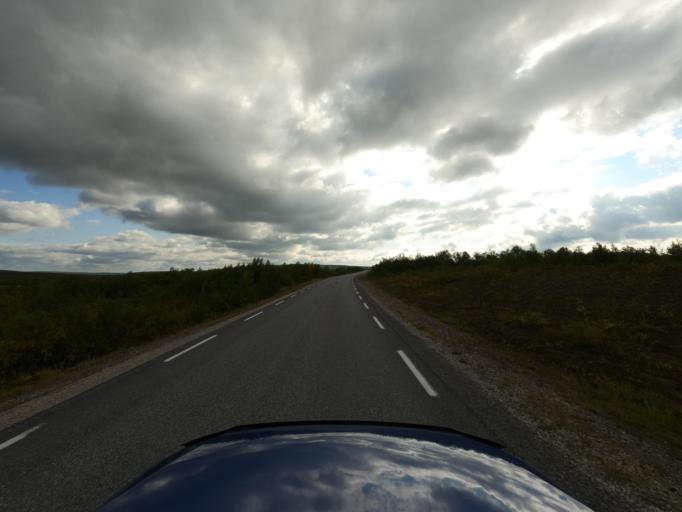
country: NO
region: Finnmark Fylke
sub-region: Porsanger
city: Lakselv
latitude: 69.3724
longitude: 24.2723
